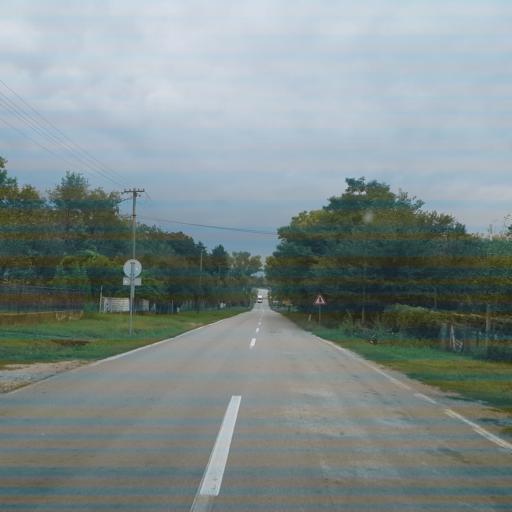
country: RS
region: Central Serbia
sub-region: Nisavski Okrug
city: Razanj
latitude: 43.6203
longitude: 21.5793
